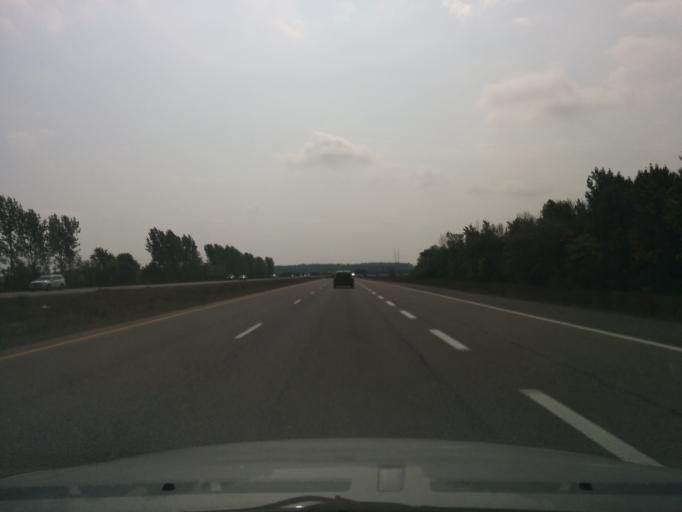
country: CA
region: Ontario
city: Bells Corners
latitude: 45.3066
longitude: -75.7968
